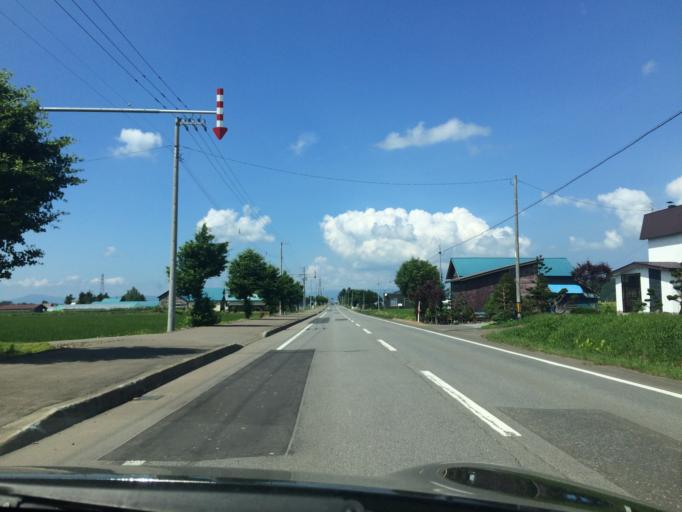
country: JP
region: Hokkaido
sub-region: Asahikawa-shi
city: Asahikawa
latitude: 43.7502
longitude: 142.4621
